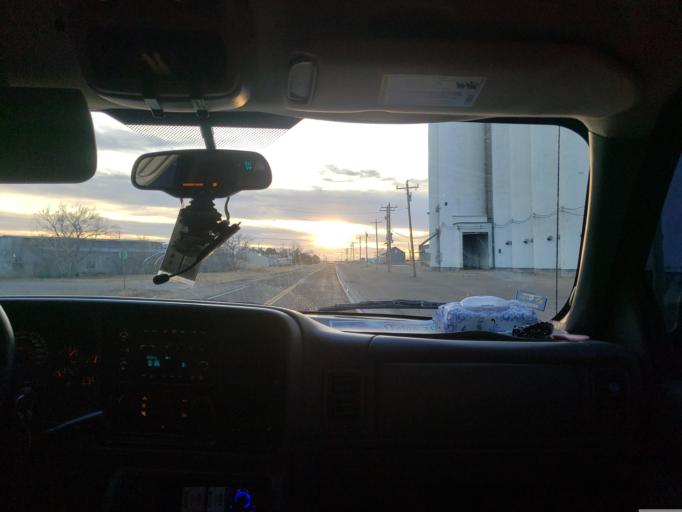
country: US
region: Oklahoma
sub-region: Cimarron County
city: Boise City
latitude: 36.8120
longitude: -102.2511
